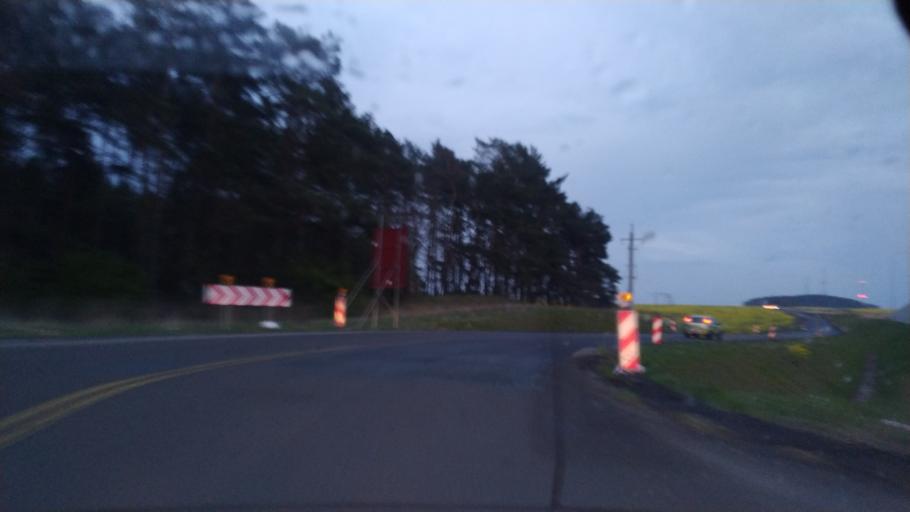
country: PL
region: Greater Poland Voivodeship
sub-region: Powiat pilski
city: Szydlowo
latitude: 53.2453
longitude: 16.6069
